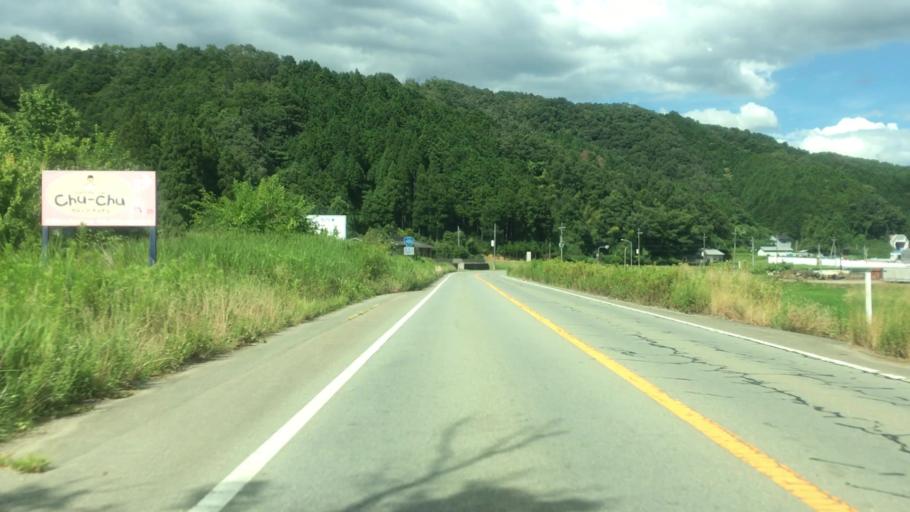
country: JP
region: Hyogo
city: Toyooka
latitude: 35.4672
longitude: 134.7571
